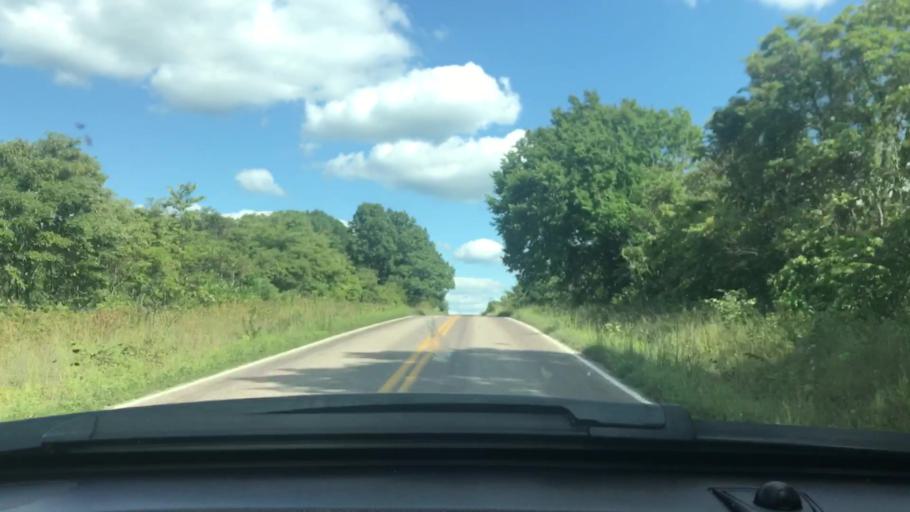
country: US
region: Missouri
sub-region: Wright County
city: Hartville
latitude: 37.3766
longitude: -92.3768
